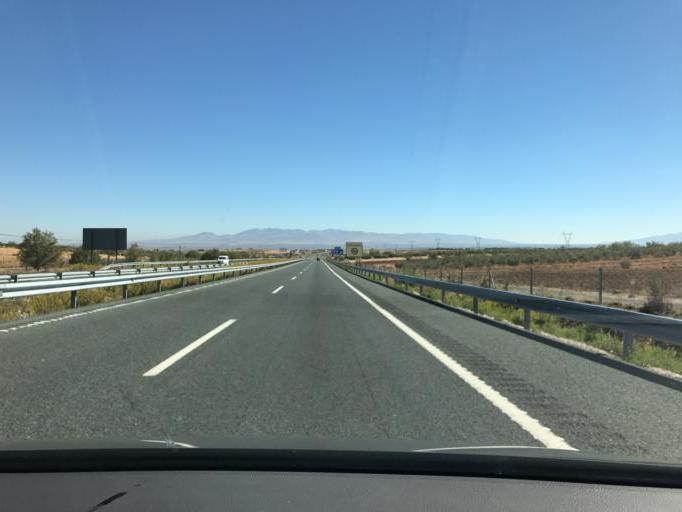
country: ES
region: Andalusia
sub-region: Provincia de Granada
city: Diezma
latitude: 37.3210
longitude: -3.3068
